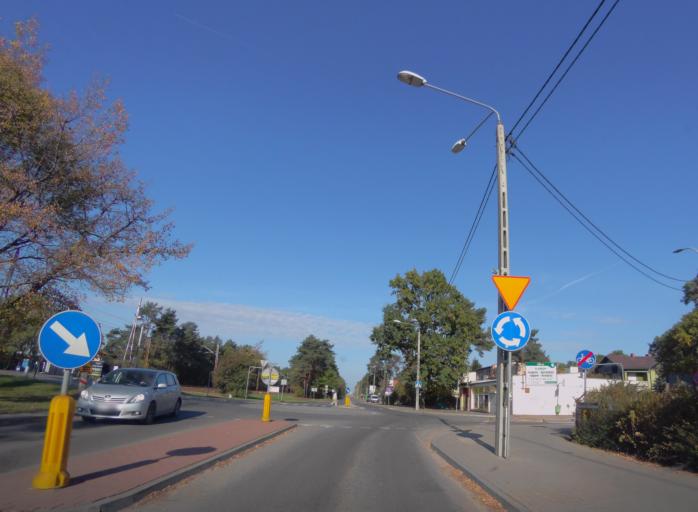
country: PL
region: Masovian Voivodeship
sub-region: Powiat otwocki
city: Jozefow
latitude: 52.1374
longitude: 21.2358
